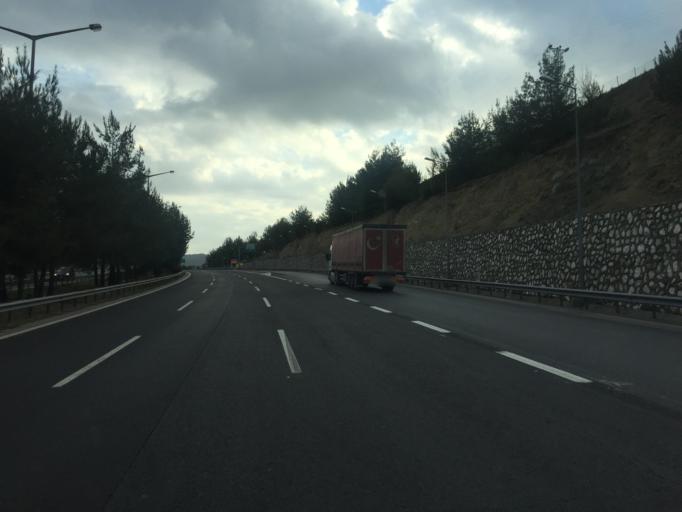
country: TR
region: Mersin
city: Camliyayla
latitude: 37.1959
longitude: 34.8309
